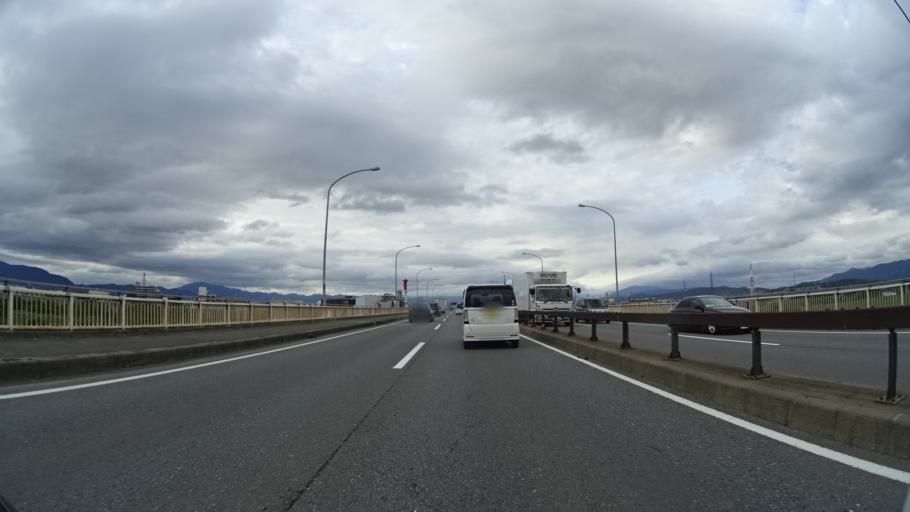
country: JP
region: Kyoto
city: Yawata
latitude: 34.9171
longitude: 135.7446
